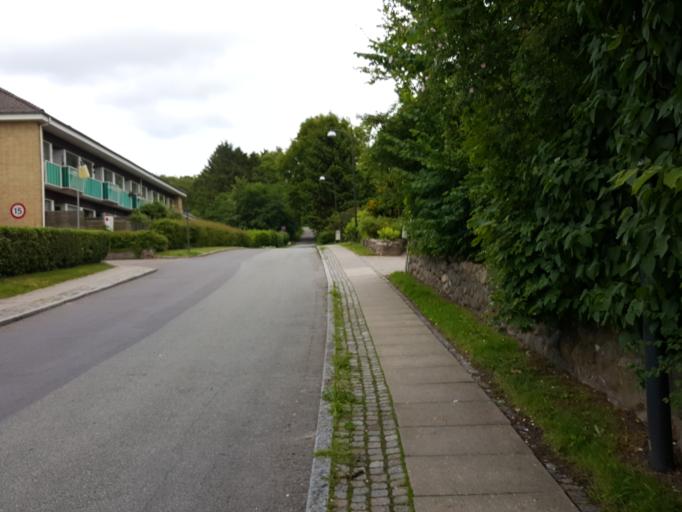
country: DK
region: Capital Region
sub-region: Rudersdal Kommune
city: Birkerod
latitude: 55.8457
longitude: 12.4385
